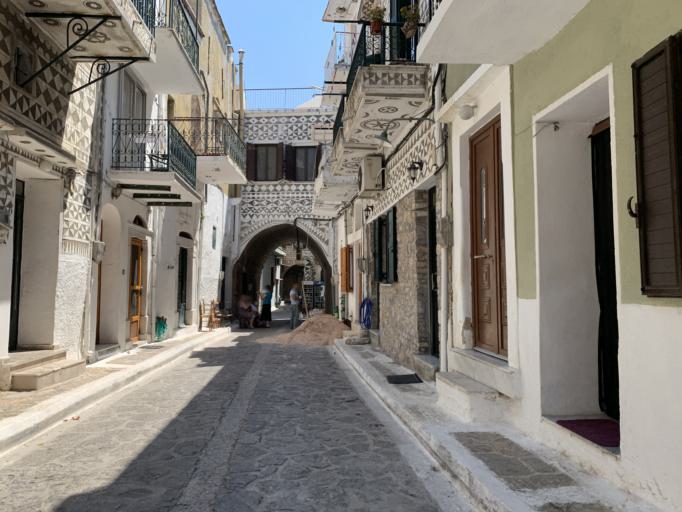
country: GR
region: North Aegean
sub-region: Chios
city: Thymiana
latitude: 38.2272
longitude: 25.9982
